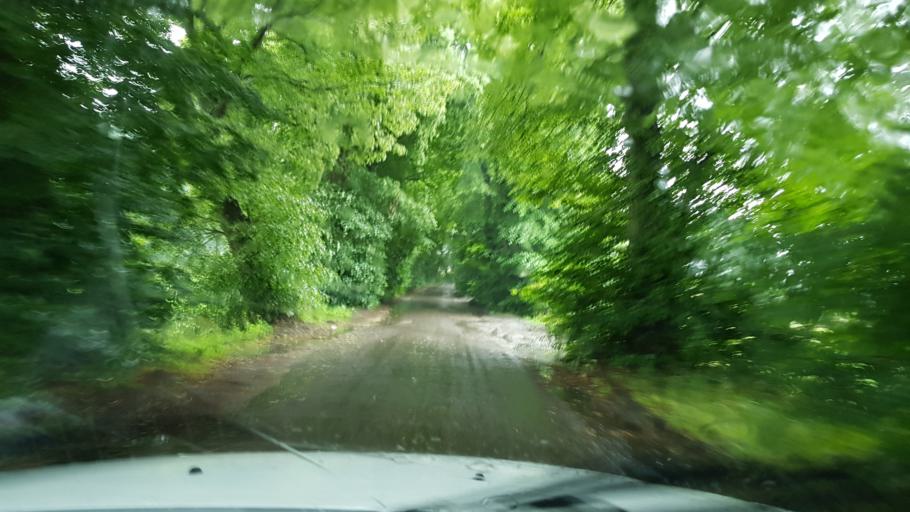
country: PL
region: West Pomeranian Voivodeship
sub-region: Powiat kolobrzeski
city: Grzybowo
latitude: 54.0701
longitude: 15.5051
